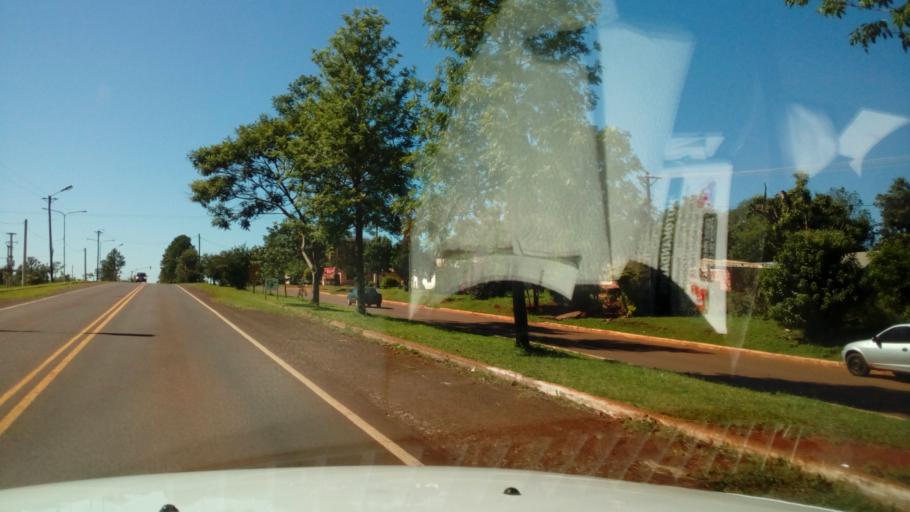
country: AR
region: Misiones
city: Bonpland
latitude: -27.4774
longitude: -55.4763
